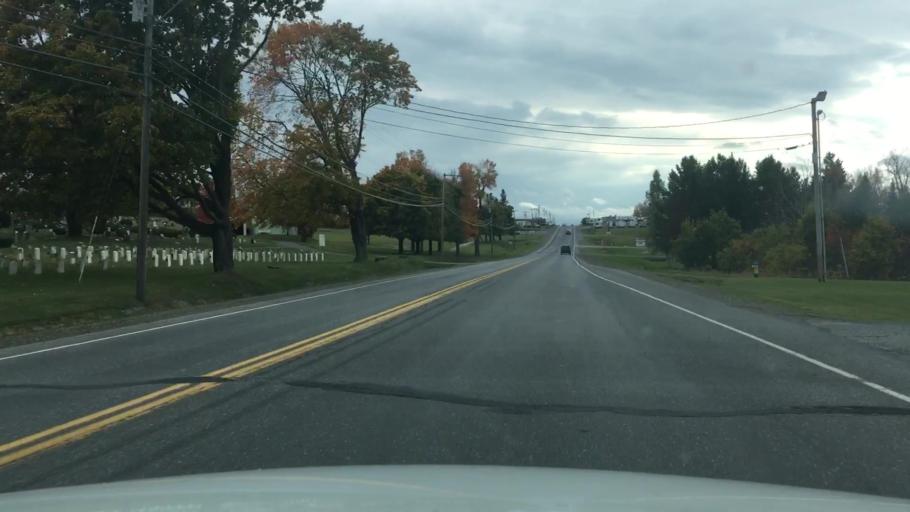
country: US
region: Maine
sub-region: Aroostook County
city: Presque Isle
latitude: 46.6640
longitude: -68.0097
